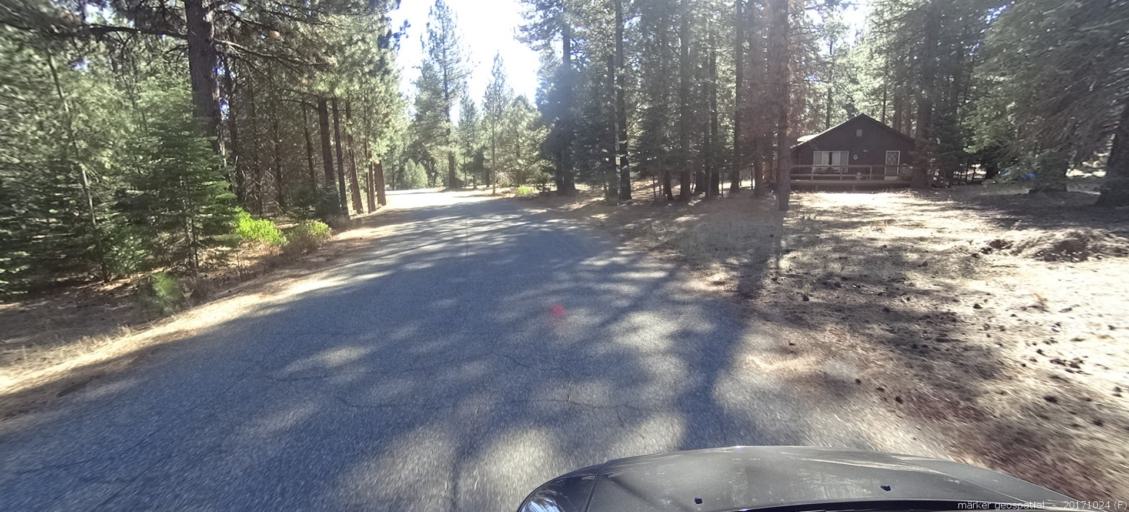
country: US
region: California
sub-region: Shasta County
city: Burney
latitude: 40.6511
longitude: -121.4630
